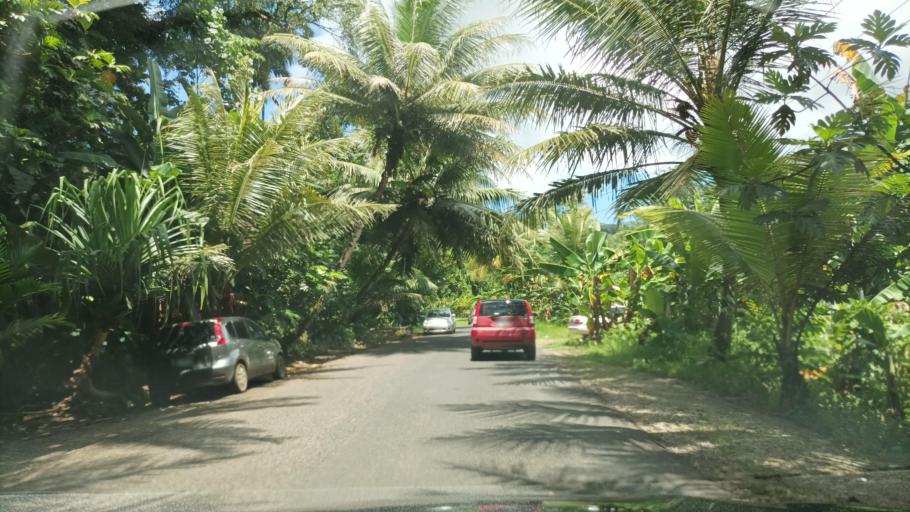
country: FM
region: Pohnpei
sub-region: Kolonia Municipality
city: Kolonia
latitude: 6.9522
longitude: 158.2322
